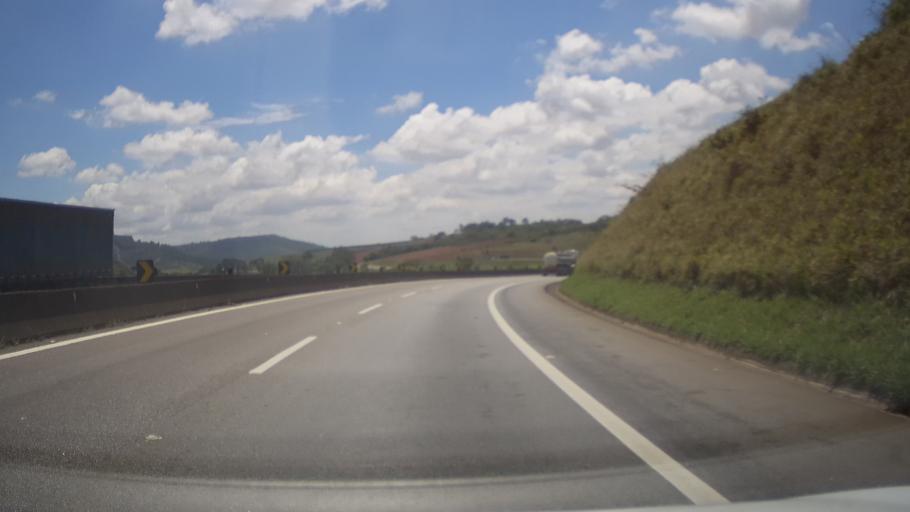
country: BR
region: Minas Gerais
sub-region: Campanha
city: Campanha
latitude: -21.8340
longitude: -45.5033
